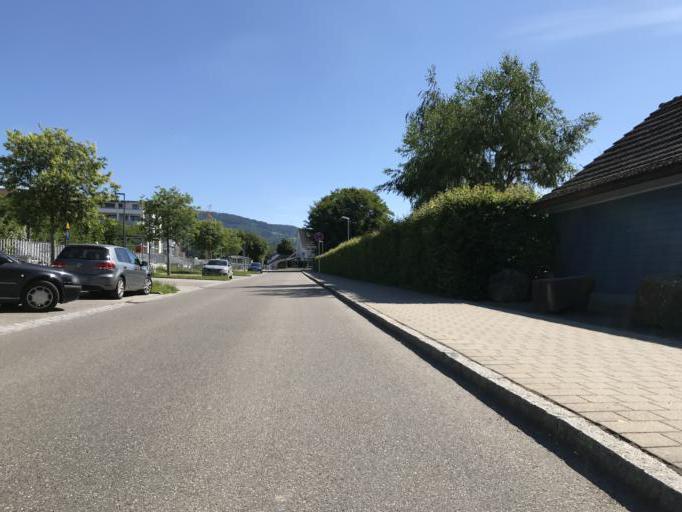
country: DE
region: Baden-Wuerttemberg
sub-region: Freiburg Region
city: Schopfheim
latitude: 47.6532
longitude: 7.8325
